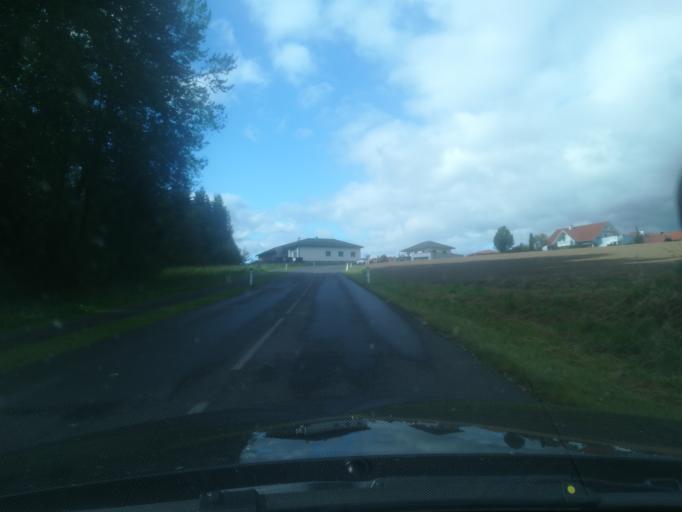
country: AT
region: Upper Austria
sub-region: Politischer Bezirk Urfahr-Umgebung
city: Herzogsdorf
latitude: 48.4314
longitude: 14.1201
